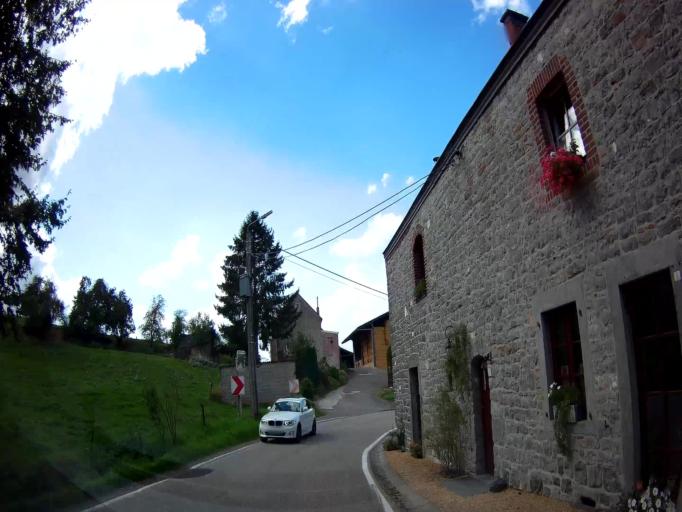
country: BE
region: Wallonia
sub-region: Province de Namur
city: Assesse
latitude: 50.3541
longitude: 4.9703
